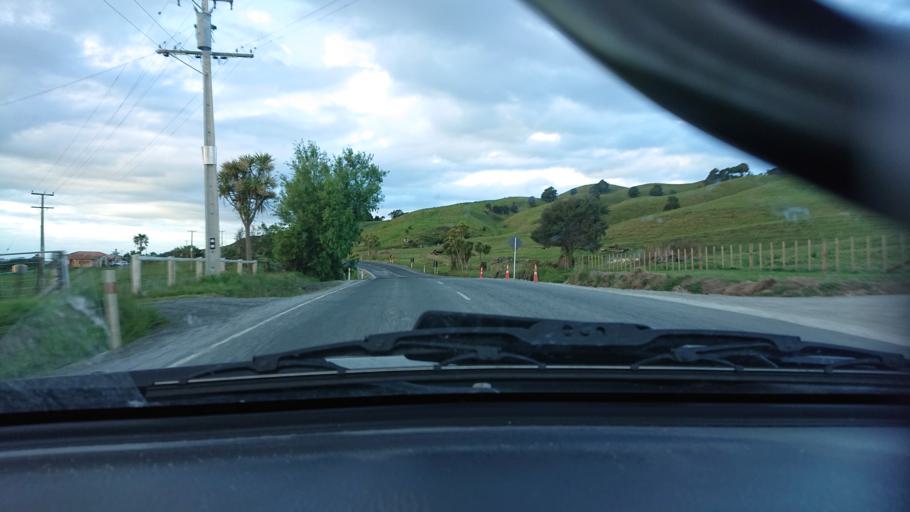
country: NZ
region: Auckland
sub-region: Auckland
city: Wellsford
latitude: -36.4489
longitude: 174.4335
